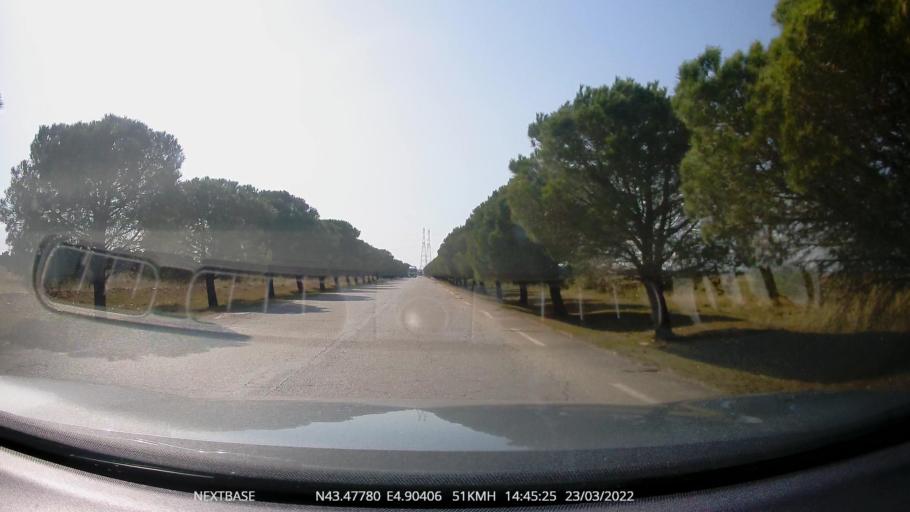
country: FR
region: Provence-Alpes-Cote d'Azur
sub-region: Departement des Bouches-du-Rhone
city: Fos-sur-Mer
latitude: 43.4781
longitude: 4.9038
